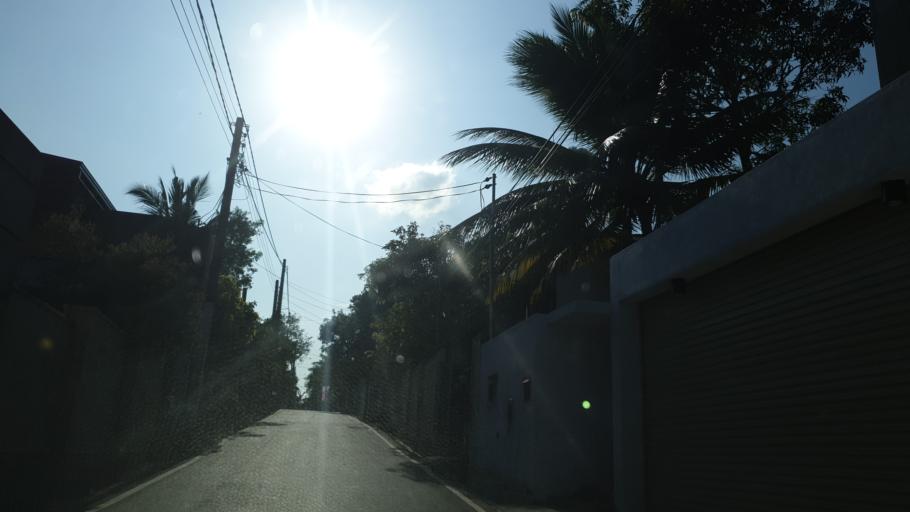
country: LK
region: Western
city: Battaramulla South
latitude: 6.8865
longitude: 79.9430
